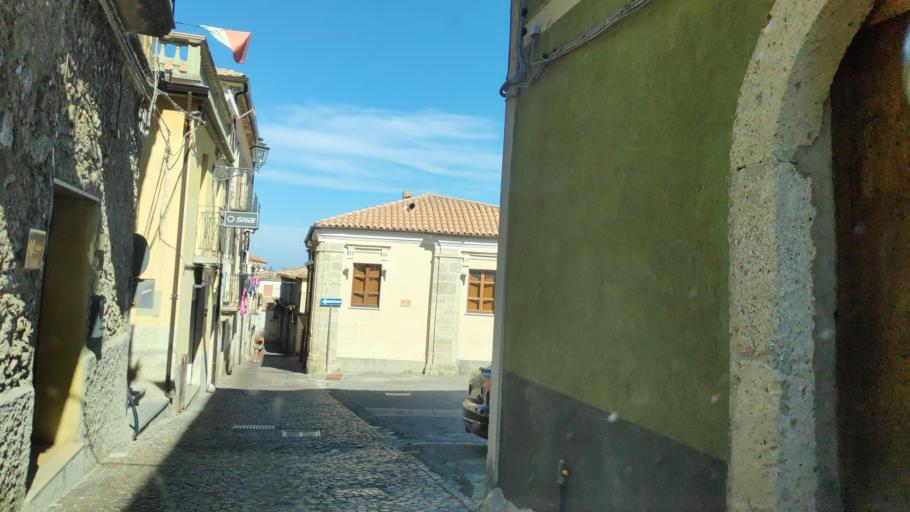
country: IT
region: Calabria
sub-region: Provincia di Catanzaro
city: Squillace
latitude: 38.7806
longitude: 16.5198
